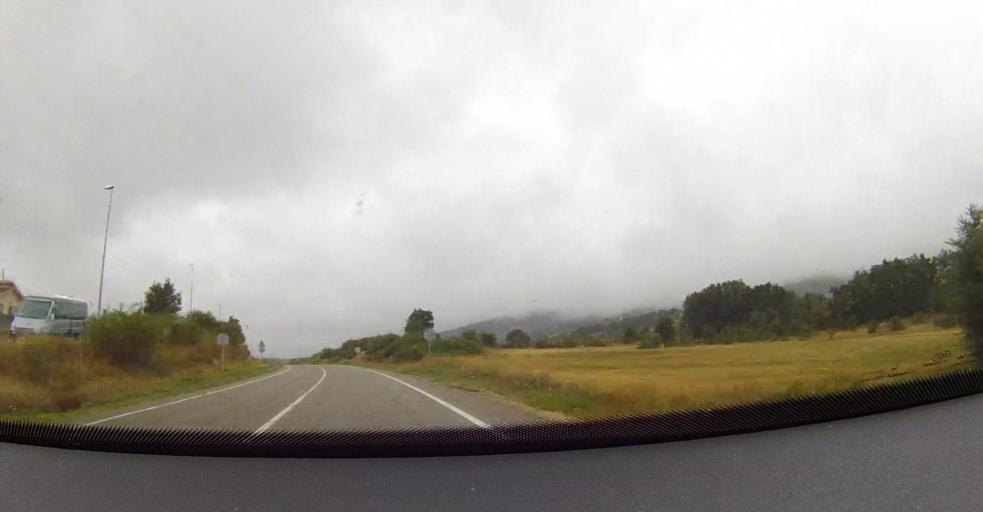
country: ES
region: Castille and Leon
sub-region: Provincia de Leon
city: Bonar
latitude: 42.8418
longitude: -5.2556
